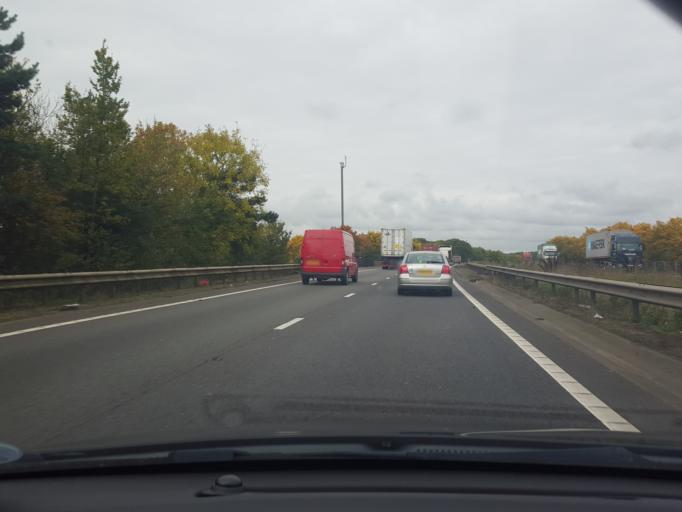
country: GB
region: England
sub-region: Suffolk
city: Bramford
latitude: 52.1029
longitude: 1.1076
